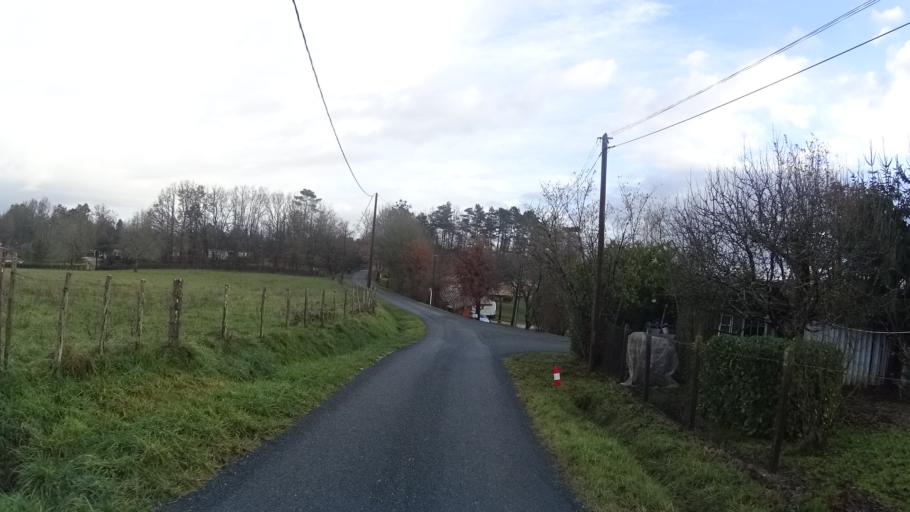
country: FR
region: Aquitaine
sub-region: Departement de la Dordogne
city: Antonne-et-Trigonant
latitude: 45.2157
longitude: 0.8815
